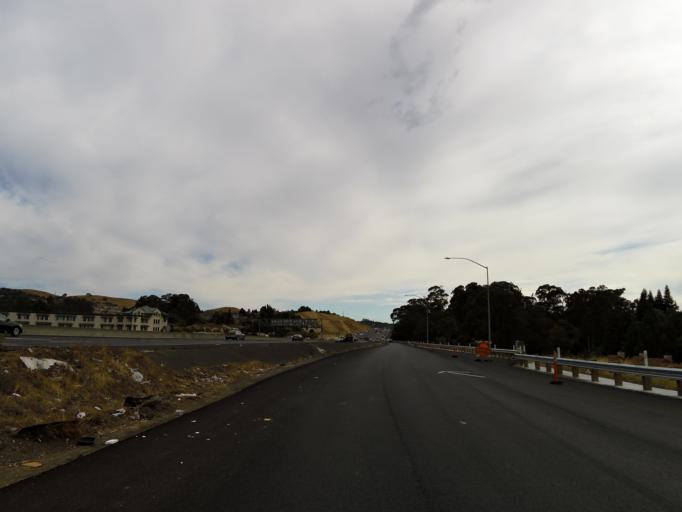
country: US
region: California
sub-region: Contra Costa County
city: Hercules
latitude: 38.0114
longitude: -122.2732
